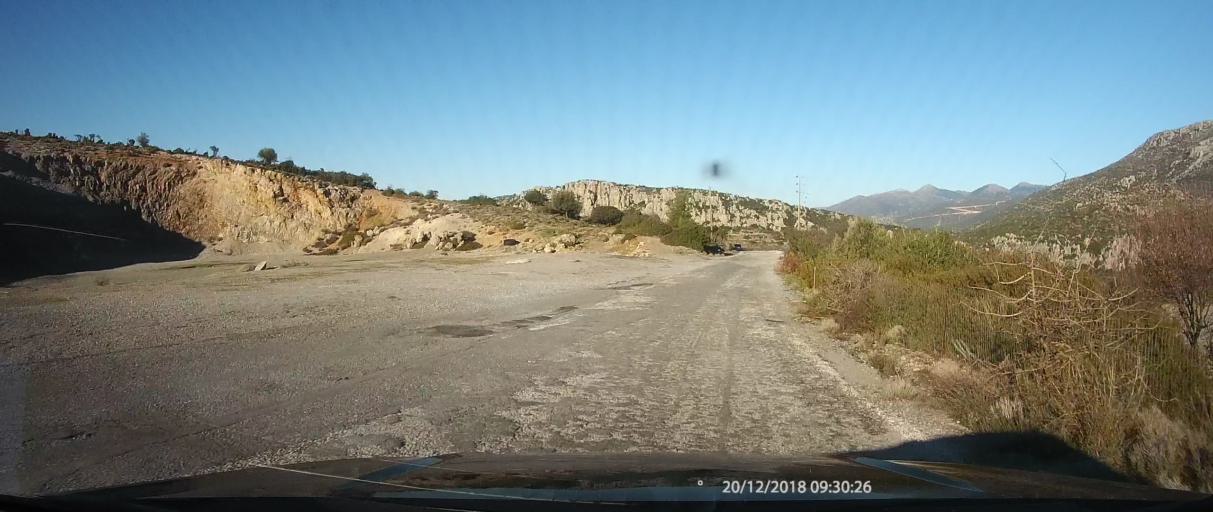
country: GR
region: Peloponnese
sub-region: Nomos Lakonias
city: Kato Glikovrisi
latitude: 36.9527
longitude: 22.8479
